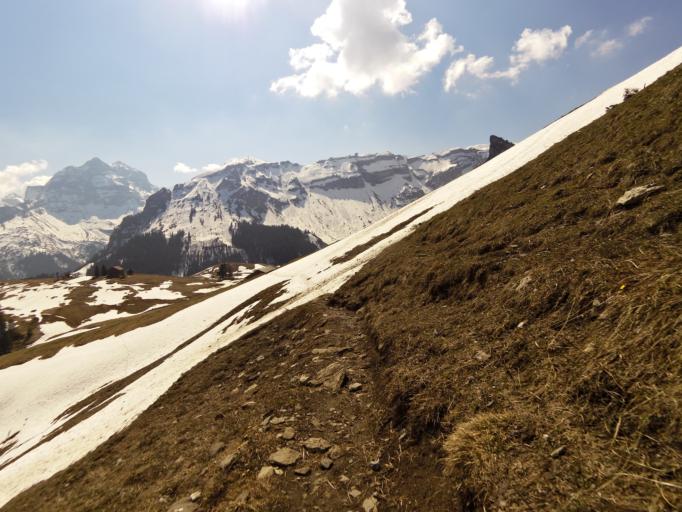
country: CH
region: Nidwalden
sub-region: Nidwalden
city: Emmetten
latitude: 46.9049
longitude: 8.4969
